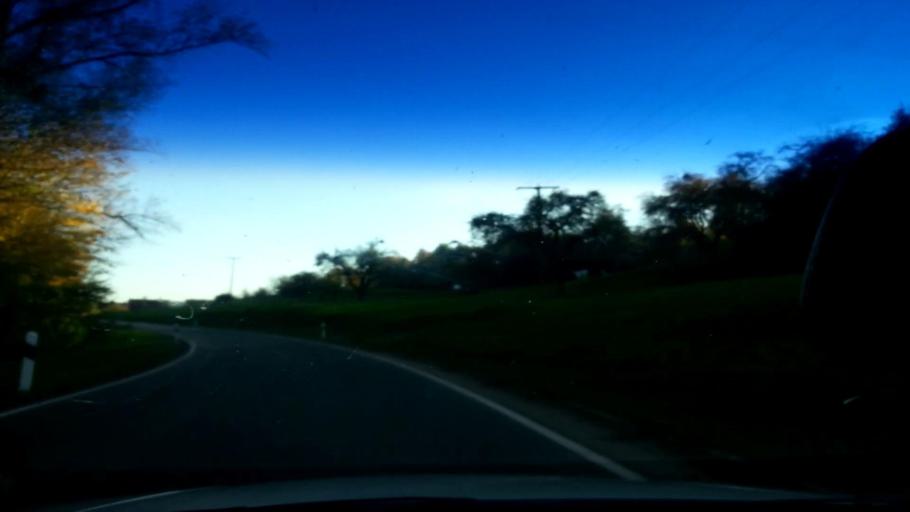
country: DE
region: Bavaria
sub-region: Upper Franconia
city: Rattelsdorf
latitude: 50.0077
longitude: 10.8731
